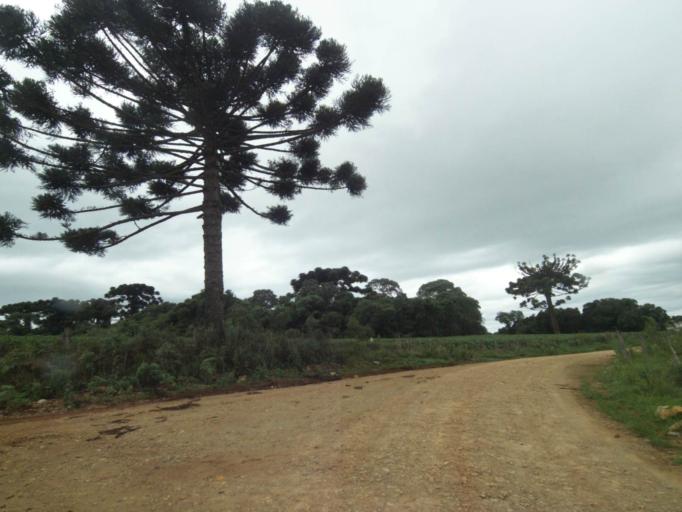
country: BR
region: Rio Grande do Sul
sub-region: Lagoa Vermelha
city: Lagoa Vermelha
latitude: -28.1961
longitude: -51.5377
